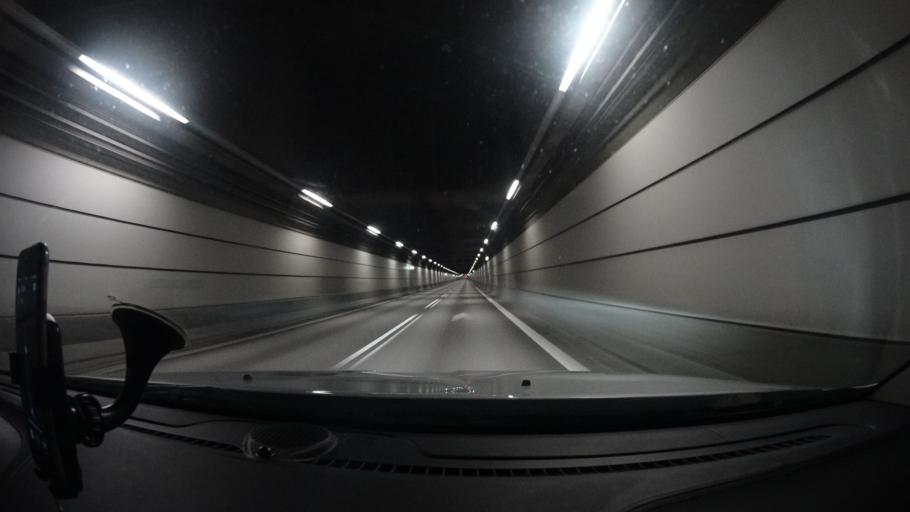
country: DK
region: Capital Region
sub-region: Dragor Kommune
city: Dragor
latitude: 55.6308
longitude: 12.6794
